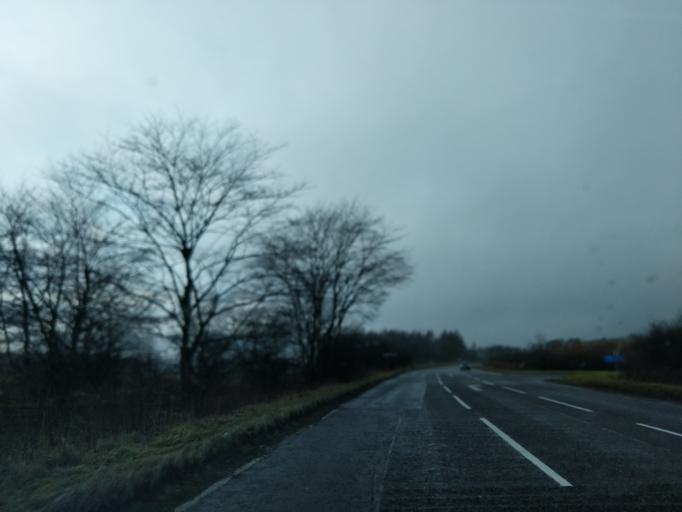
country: GB
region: Scotland
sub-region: Perth and Kinross
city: Kinross
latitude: 56.2049
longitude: -3.4690
